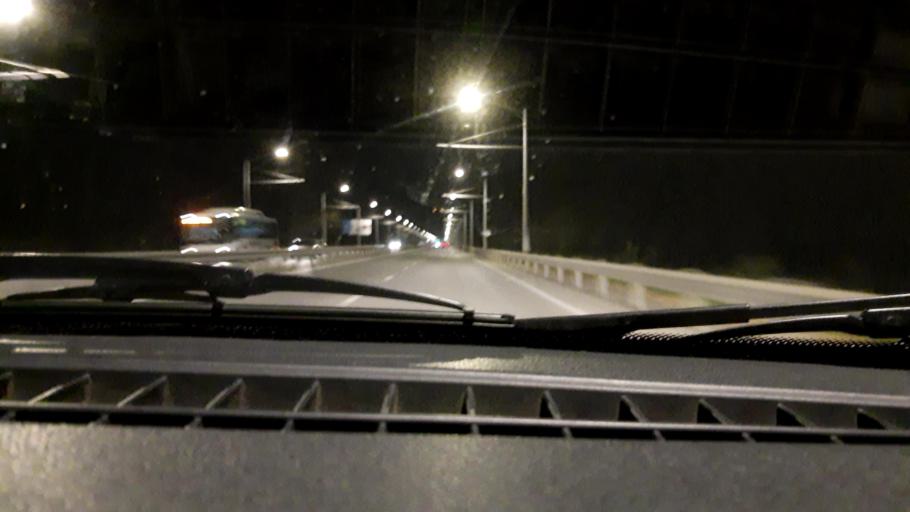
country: RU
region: Bashkortostan
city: Ufa
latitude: 54.7675
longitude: 55.9294
